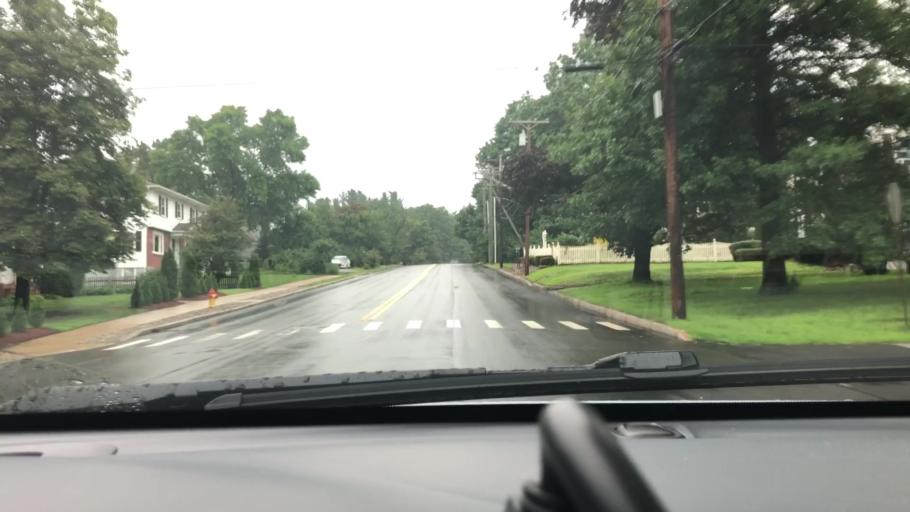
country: US
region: New Hampshire
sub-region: Hillsborough County
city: Manchester
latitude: 43.0162
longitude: -71.4618
